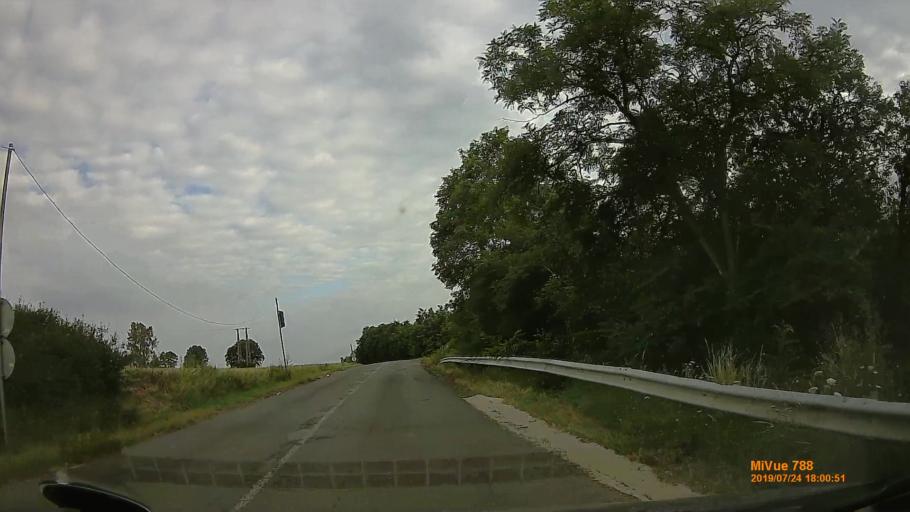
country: HU
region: Borsod-Abauj-Zemplen
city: Encs
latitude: 48.3160
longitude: 21.1658
